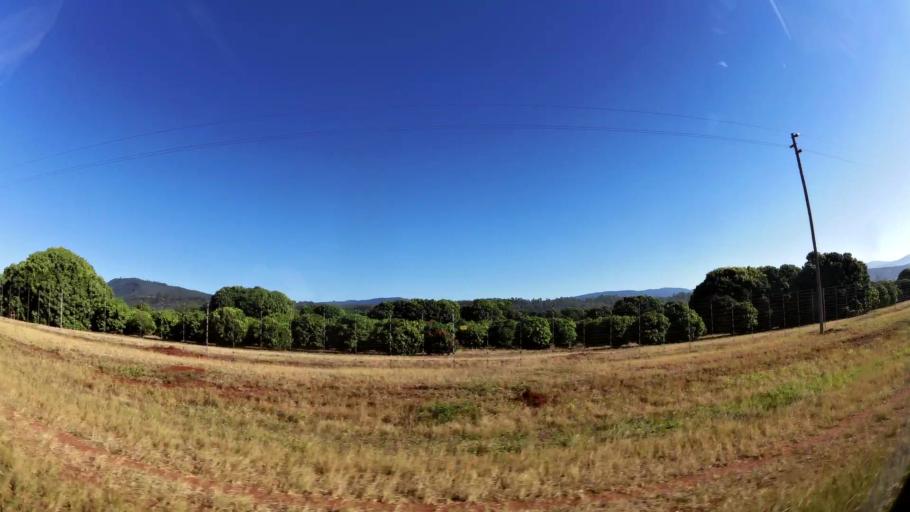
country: ZA
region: Limpopo
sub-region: Mopani District Municipality
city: Tzaneen
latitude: -23.8513
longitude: 30.1161
